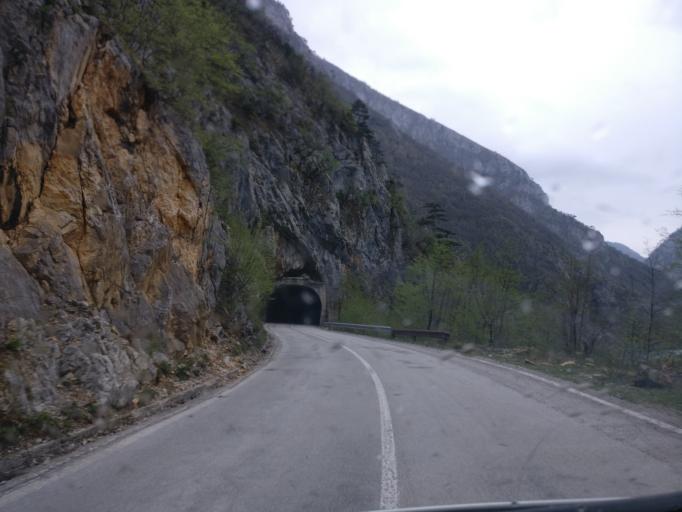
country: ME
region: Opstina Pluzine
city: Pluzine
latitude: 43.2371
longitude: 18.8432
